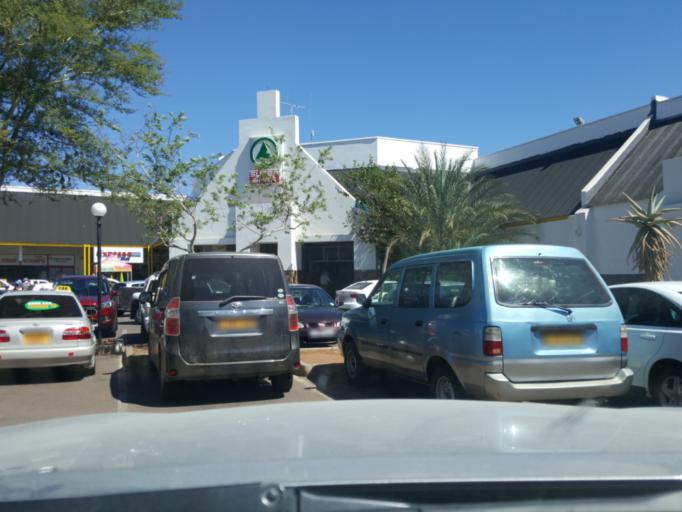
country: BW
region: South East
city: Gaborone
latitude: -24.6869
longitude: 25.8823
